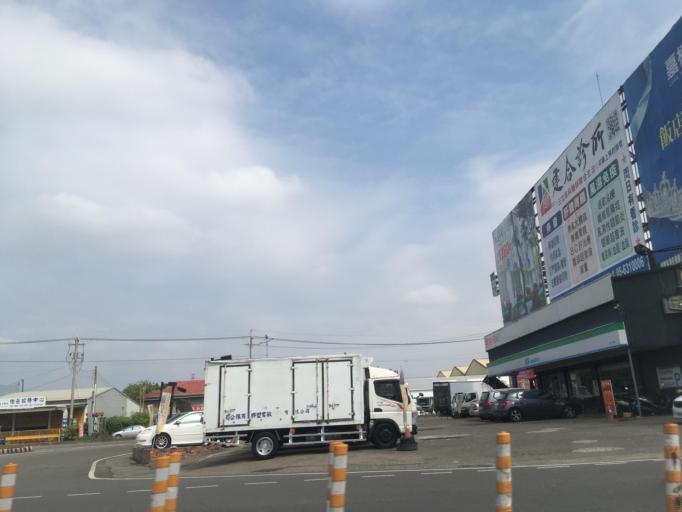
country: TW
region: Taiwan
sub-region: Yunlin
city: Douliu
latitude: 23.6942
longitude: 120.4640
